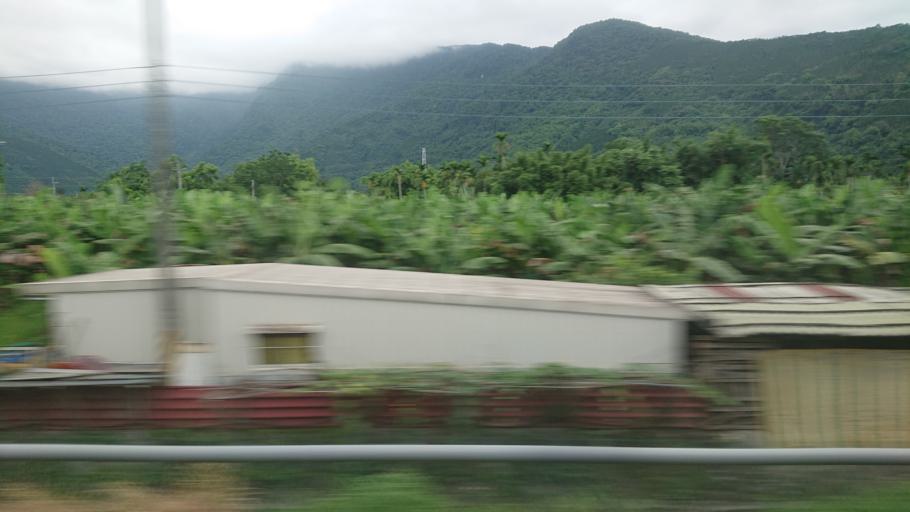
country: TW
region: Taiwan
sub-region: Hualien
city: Hualian
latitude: 23.7550
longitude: 121.4512
